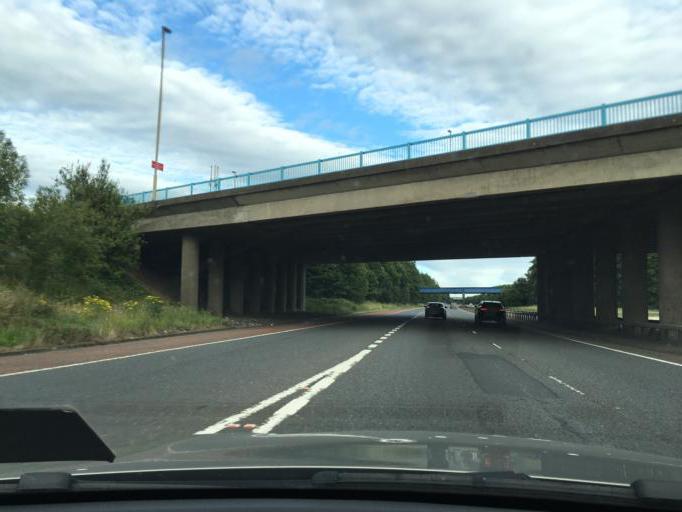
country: GB
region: Northern Ireland
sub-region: Antrim Borough
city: Templepatrick
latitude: 54.7102
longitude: -6.0695
